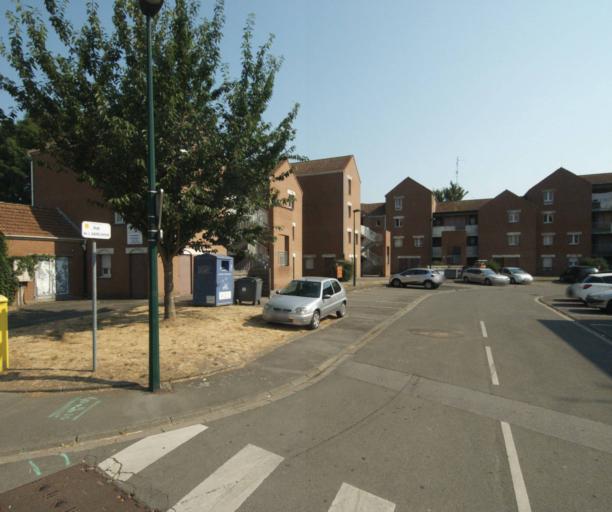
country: FR
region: Nord-Pas-de-Calais
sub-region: Departement du Nord
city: Quesnoy-sur-Deule
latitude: 50.7093
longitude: 3.0005
